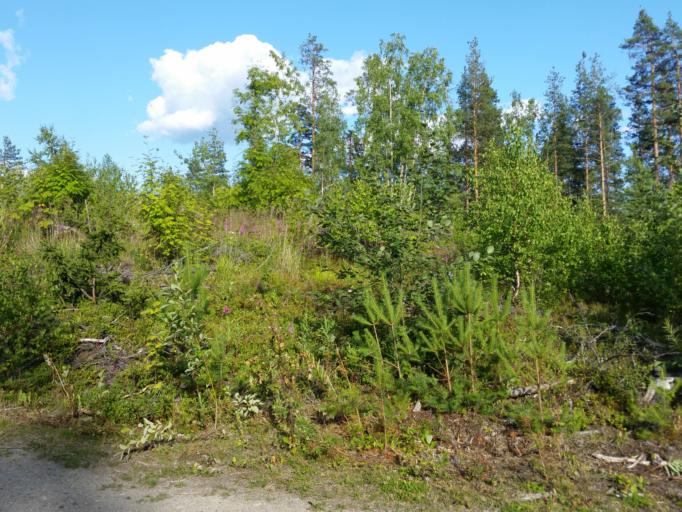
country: FI
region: Southern Savonia
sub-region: Savonlinna
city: Sulkava
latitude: 61.7783
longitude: 28.4218
